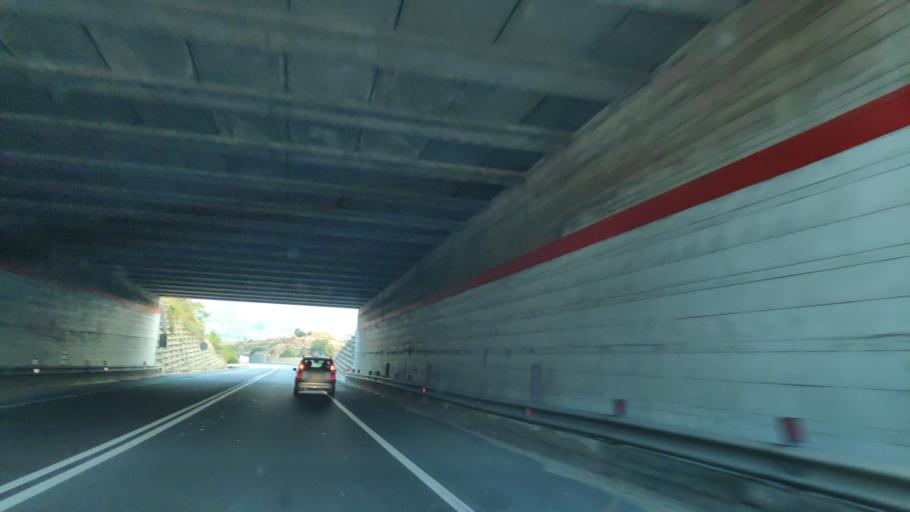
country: IT
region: Calabria
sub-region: Provincia di Catanzaro
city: Soverato Superiore
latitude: 38.6960
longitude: 16.5382
